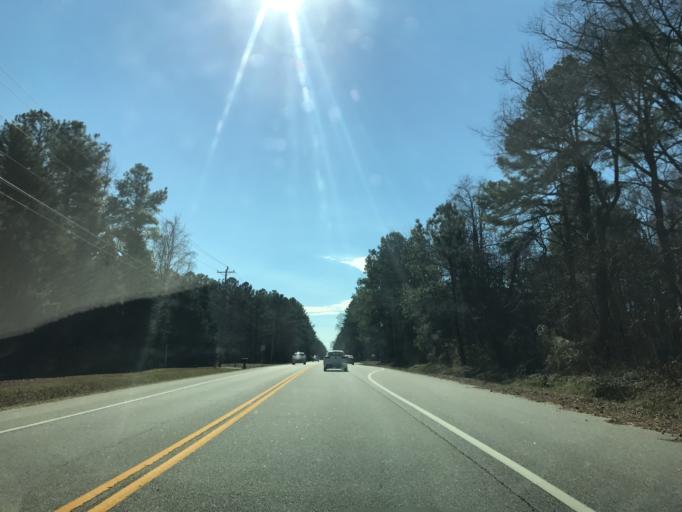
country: US
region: Maryland
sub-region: Queen Anne's County
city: Stevensville
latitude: 38.9549
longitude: -76.3468
